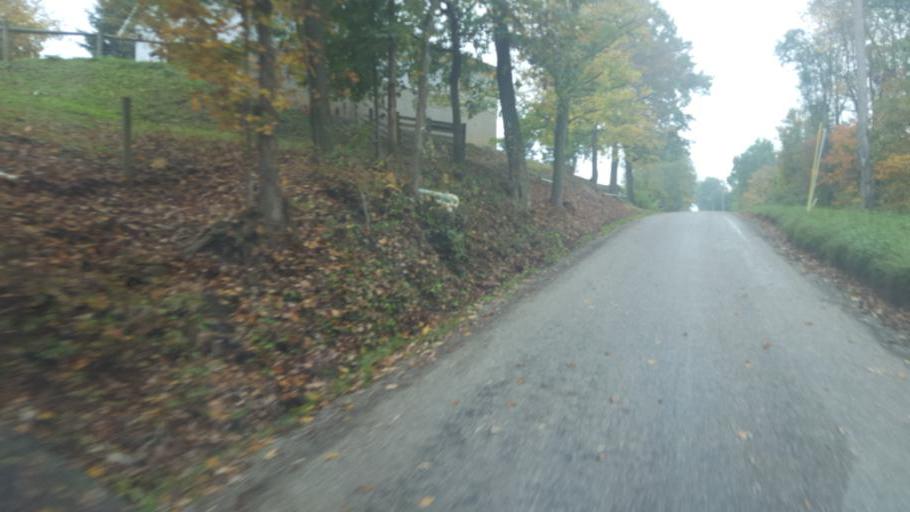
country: US
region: Ohio
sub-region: Tuscarawas County
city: Sugarcreek
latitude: 40.5748
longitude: -81.7049
